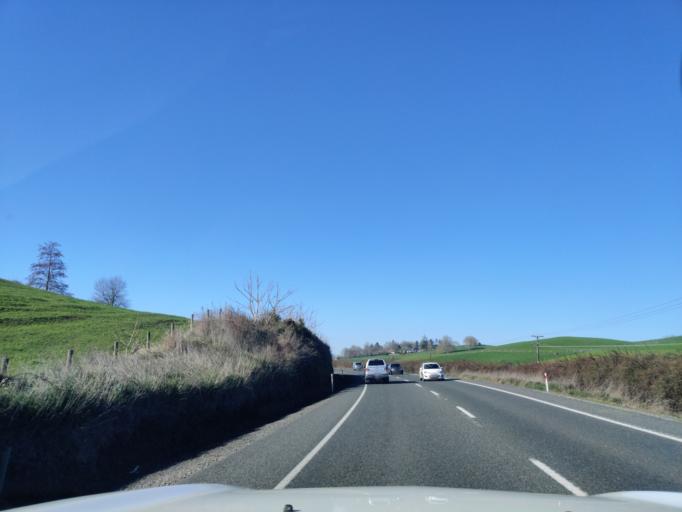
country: NZ
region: Waikato
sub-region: Matamata-Piako District
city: Matamata
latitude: -38.0055
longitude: 175.7693
